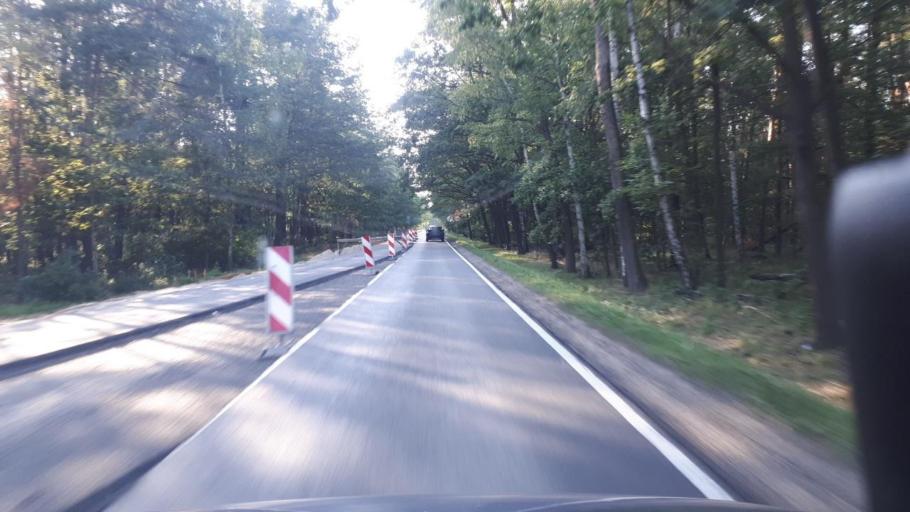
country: PL
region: Silesian Voivodeship
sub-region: Powiat lubliniecki
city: Sierakow Slaski
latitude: 50.8180
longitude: 18.5385
